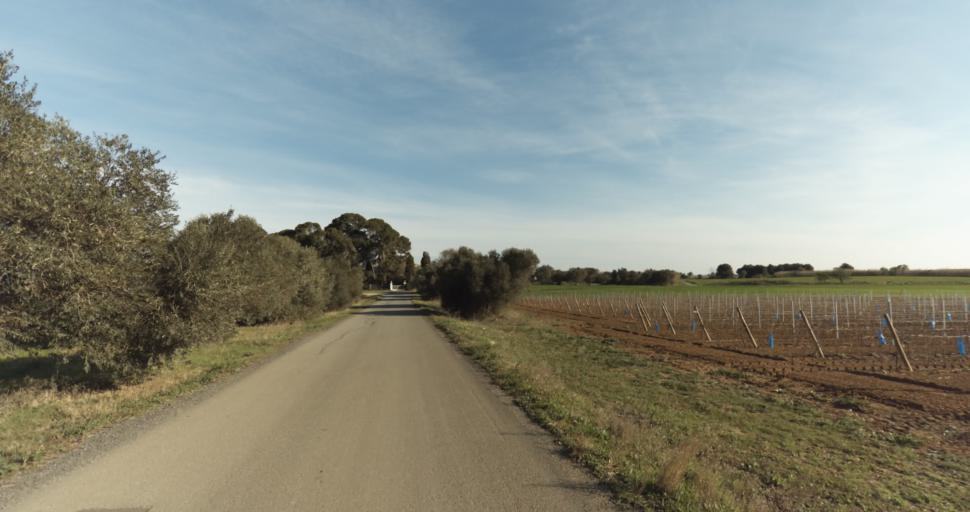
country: FR
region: Languedoc-Roussillon
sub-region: Departement de l'Herault
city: Pomerols
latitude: 43.3807
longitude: 3.5183
